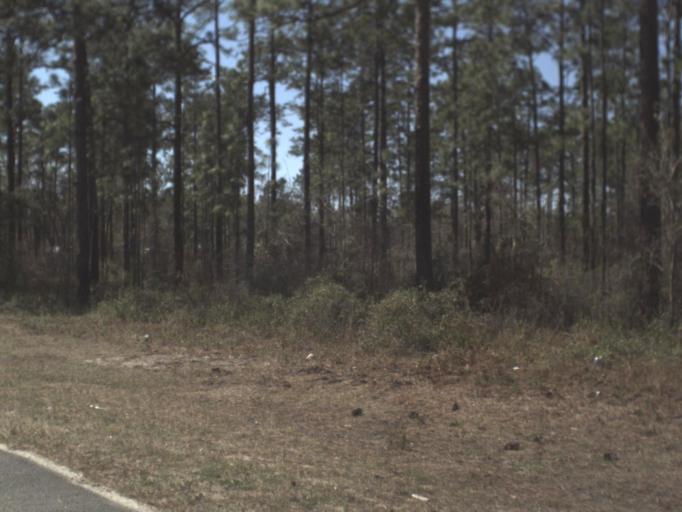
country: US
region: Florida
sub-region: Leon County
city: Woodville
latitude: 30.3332
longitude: -84.3113
